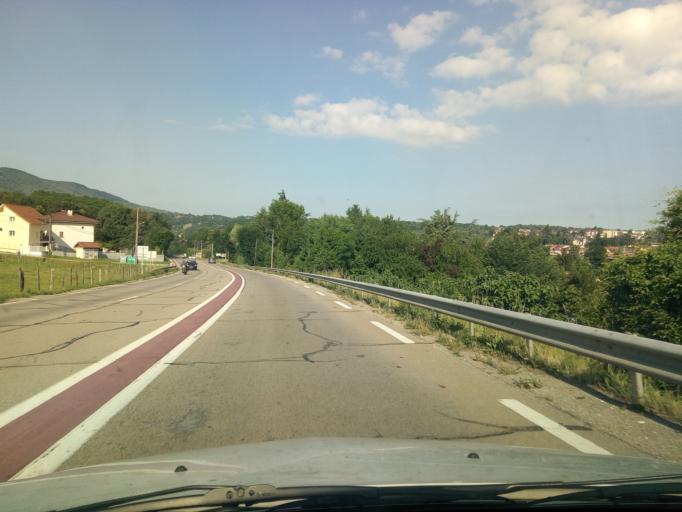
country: FR
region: Rhone-Alpes
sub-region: Departement de l'Isere
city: Rives
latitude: 45.3472
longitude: 5.5116
